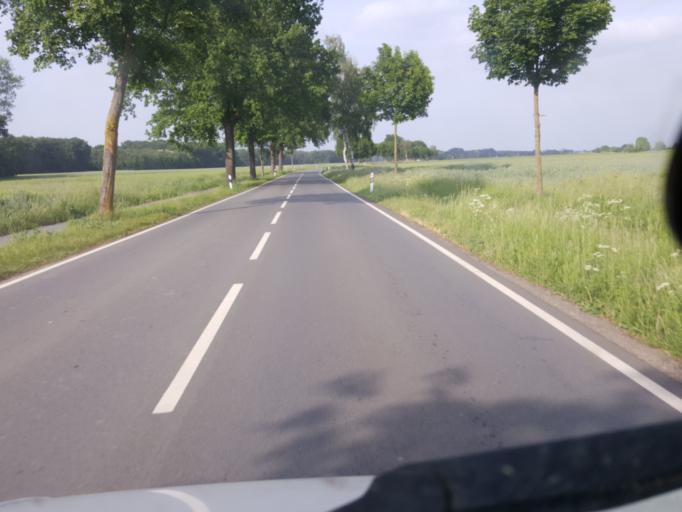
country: DE
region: Lower Saxony
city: Steyerberg
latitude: 52.5704
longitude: 9.0401
